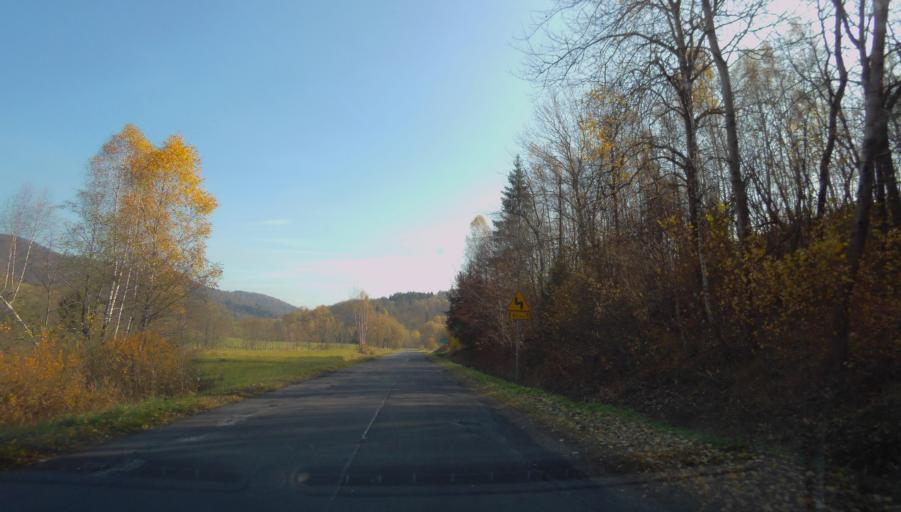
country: PL
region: Subcarpathian Voivodeship
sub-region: Powiat leski
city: Cisna
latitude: 49.2068
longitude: 22.2548
